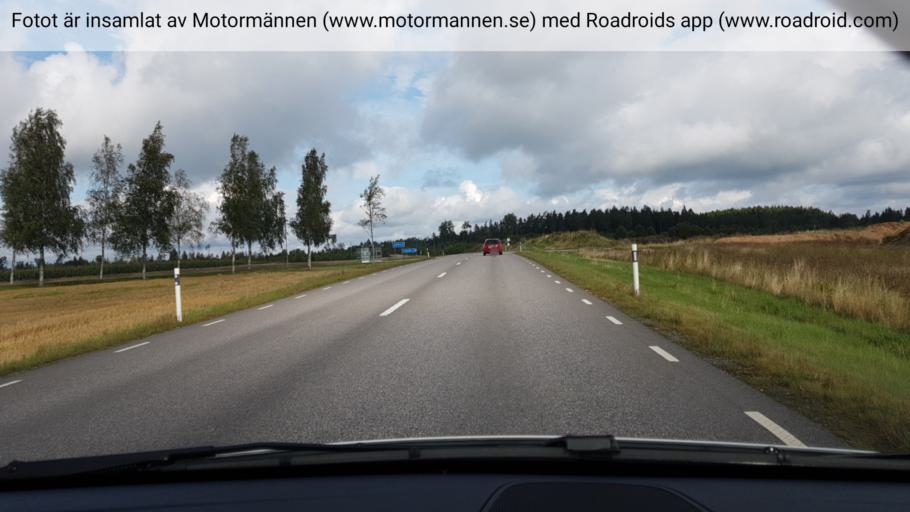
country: SE
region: Vaestra Goetaland
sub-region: Essunga Kommun
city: Nossebro
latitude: 58.1003
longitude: 12.6568
